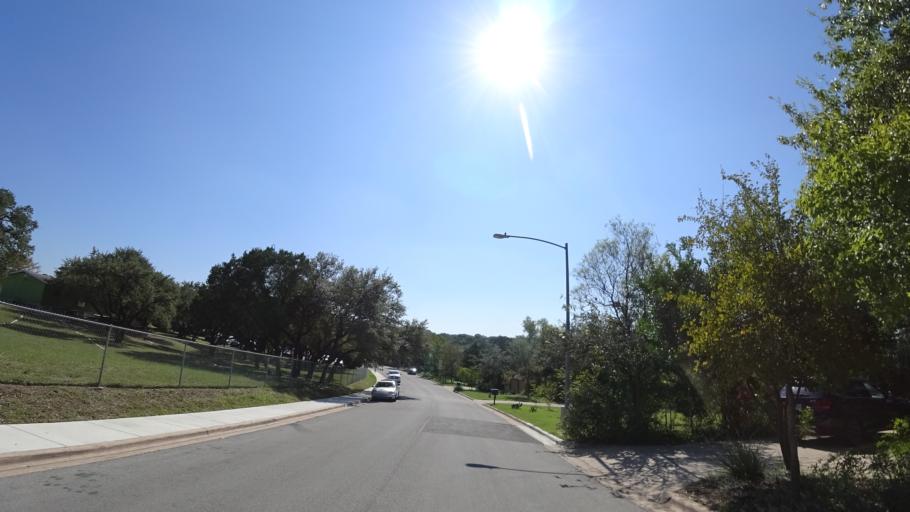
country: US
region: Texas
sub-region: Travis County
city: Rollingwood
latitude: 30.2562
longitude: -97.7836
